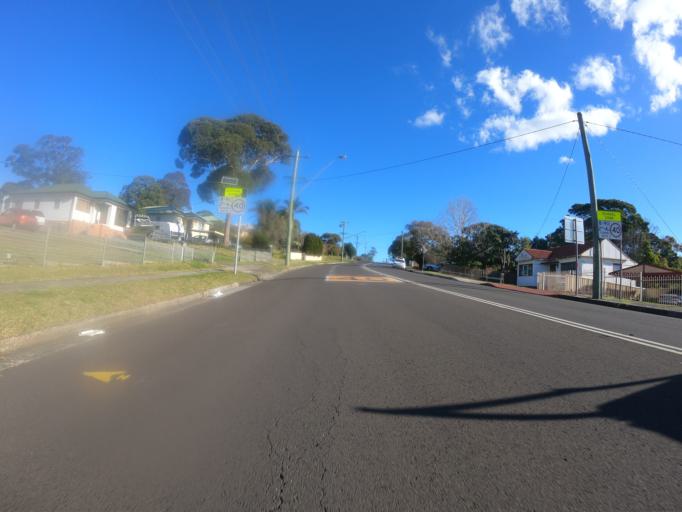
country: AU
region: New South Wales
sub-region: Wollongong
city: Cordeaux Heights
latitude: -34.4597
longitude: 150.8371
